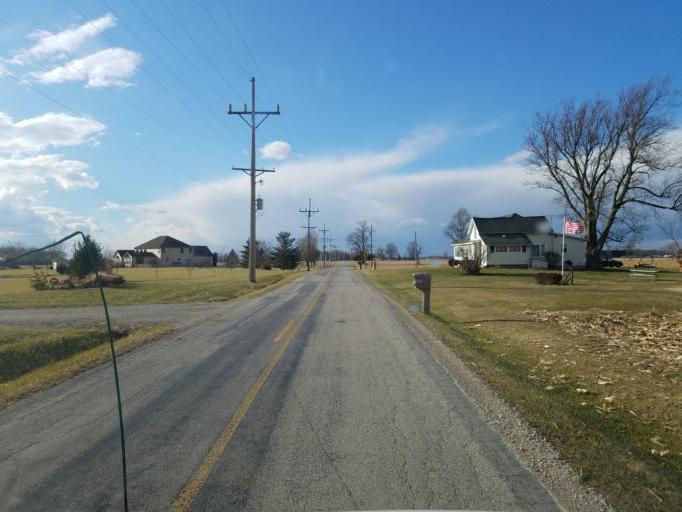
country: US
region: Ohio
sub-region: Marion County
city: Prospect
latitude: 40.4714
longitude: -83.1212
